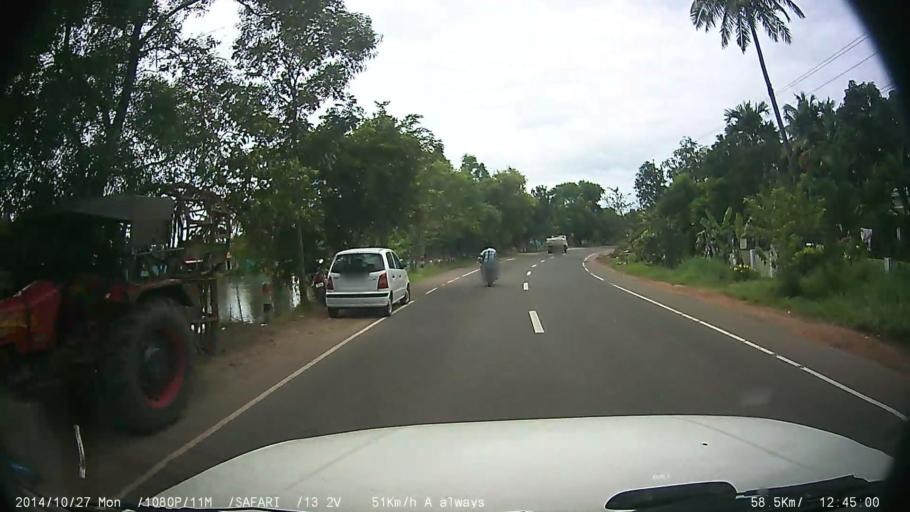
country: IN
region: Kerala
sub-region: Kottayam
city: Changanacheri
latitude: 9.4181
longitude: 76.4883
